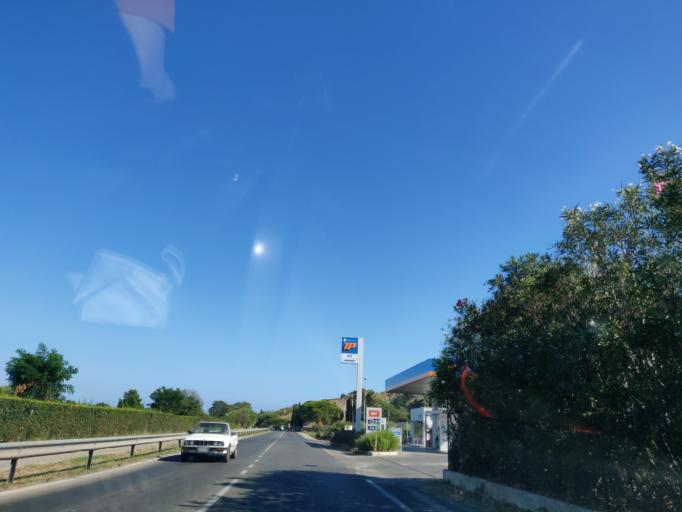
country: IT
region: Tuscany
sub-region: Provincia di Grosseto
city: Porto Ercole
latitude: 42.4260
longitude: 11.1974
